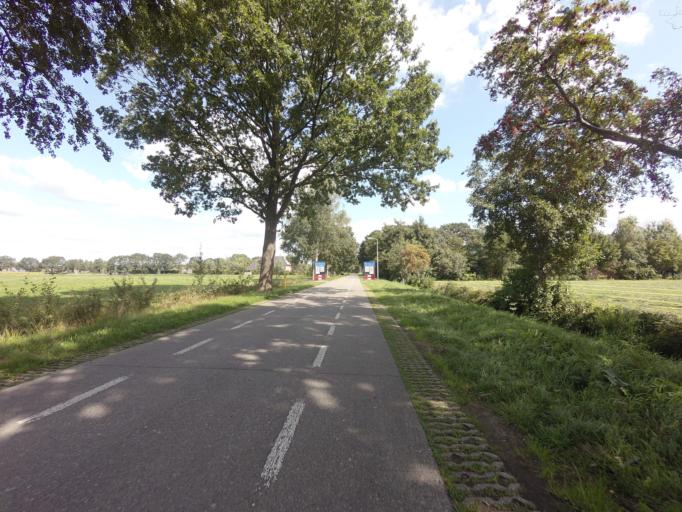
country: NL
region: Overijssel
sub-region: Gemeente Staphorst
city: Staphorst
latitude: 52.6114
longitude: 6.2608
